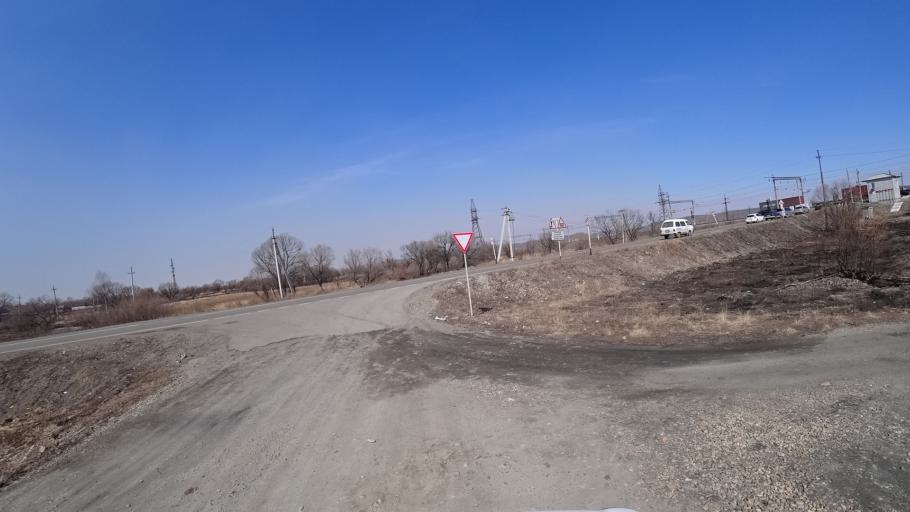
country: RU
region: Amur
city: Novobureyskiy
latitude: 49.7919
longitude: 129.8517
